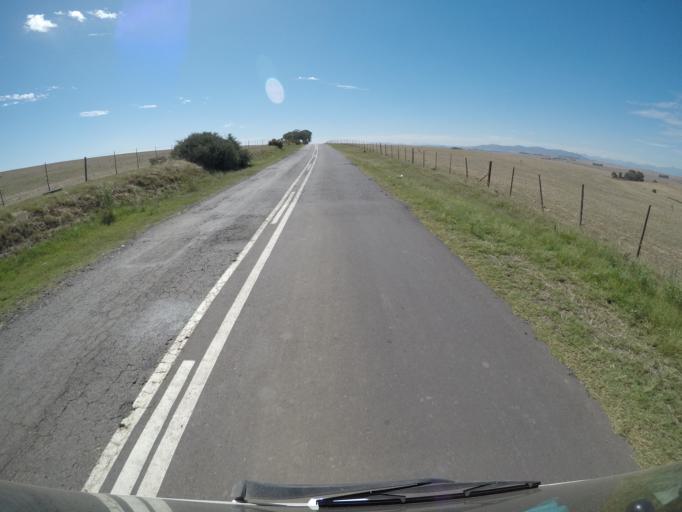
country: ZA
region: Western Cape
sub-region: City of Cape Town
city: Atlantis
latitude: -33.6948
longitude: 18.5924
